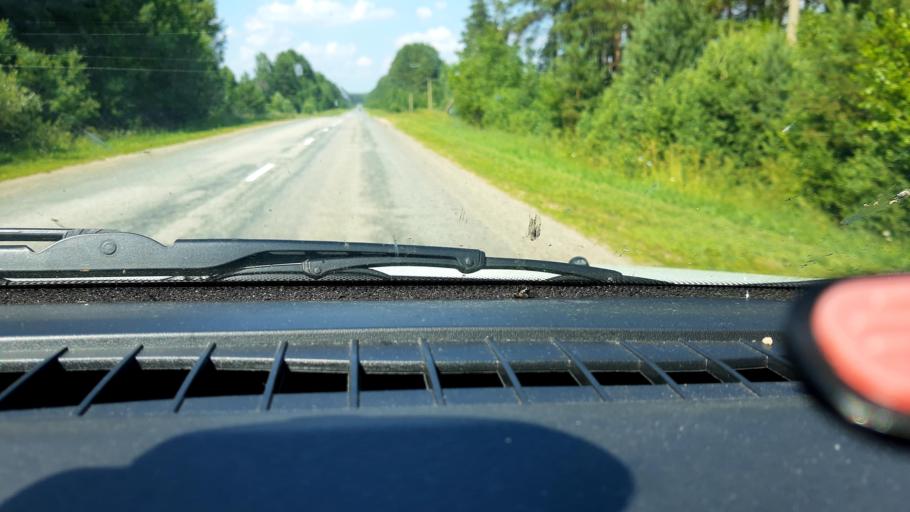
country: RU
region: Nizjnij Novgorod
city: Tonkino
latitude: 57.2822
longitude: 46.4616
